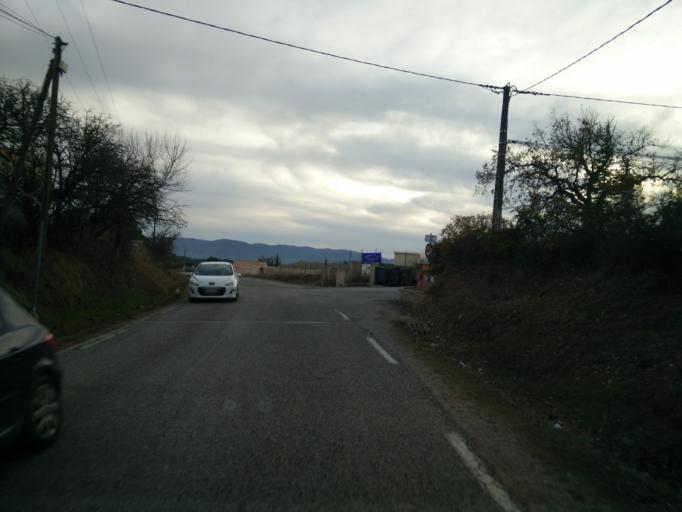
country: FR
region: Provence-Alpes-Cote d'Azur
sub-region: Departement du Var
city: Vidauban
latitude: 43.4062
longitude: 6.4290
